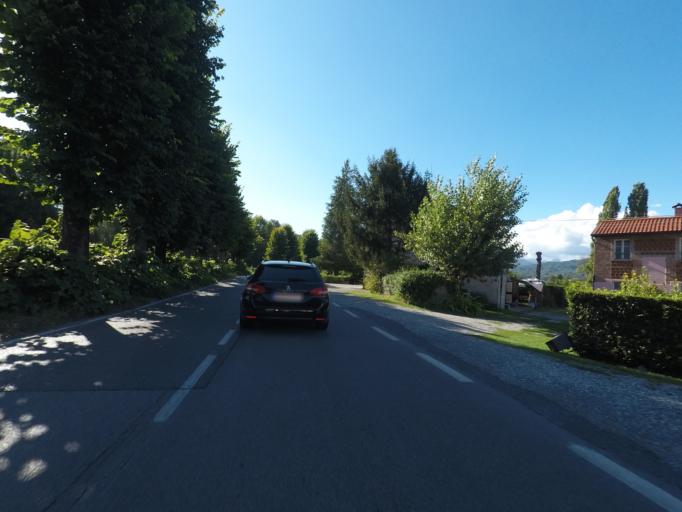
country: IT
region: Tuscany
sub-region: Provincia di Lucca
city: Lucca
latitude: 43.8766
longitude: 10.4894
